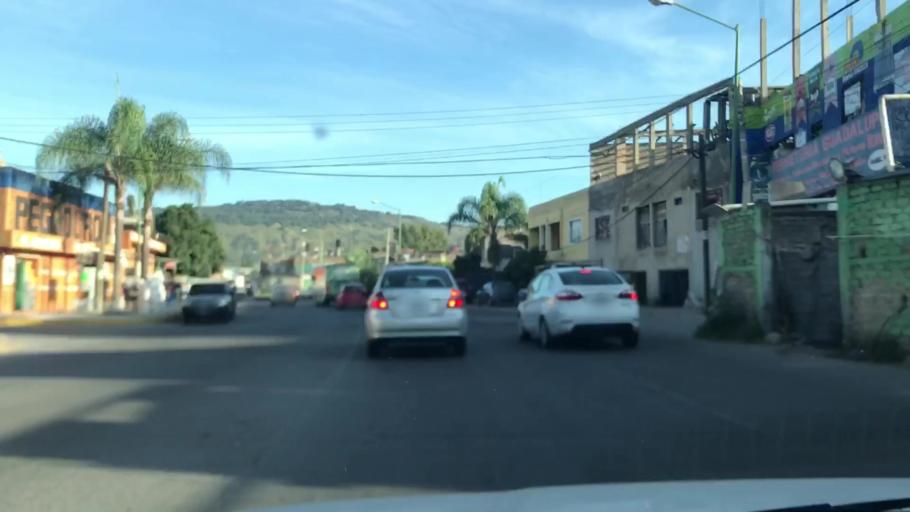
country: MX
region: Jalisco
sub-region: Tlajomulco de Zuniga
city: Palomar
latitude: 20.6316
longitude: -103.4603
